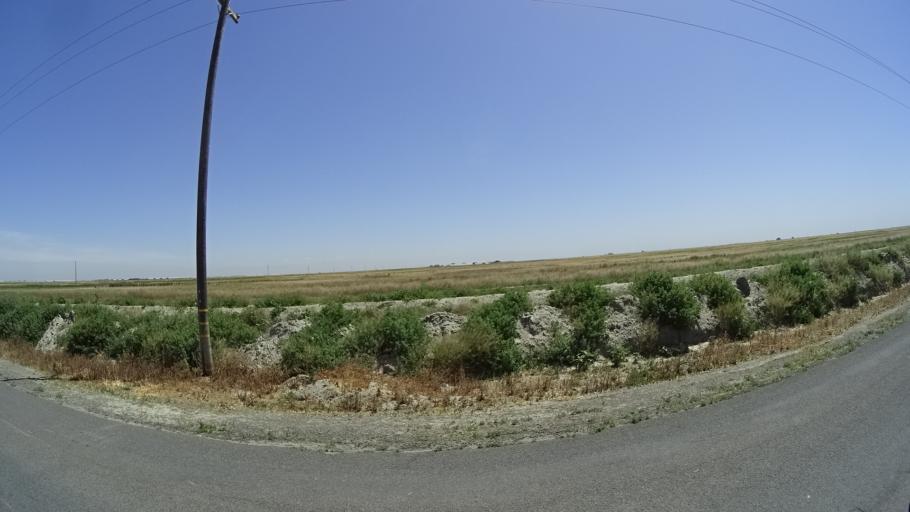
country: US
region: California
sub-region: Kings County
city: Stratford
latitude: 36.1663
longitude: -119.7174
